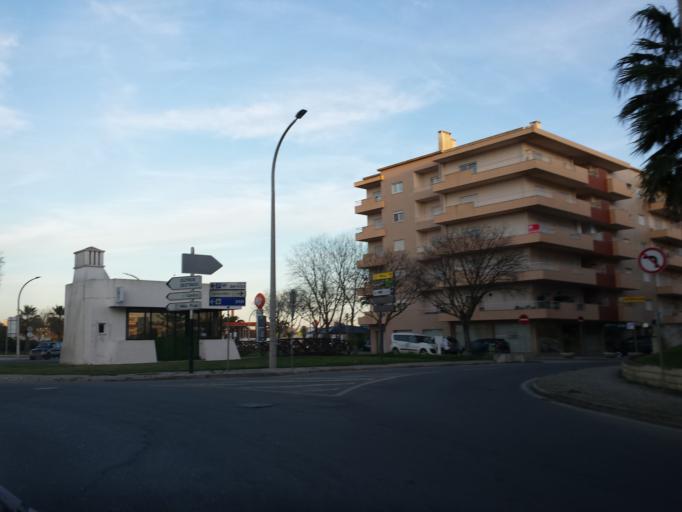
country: PT
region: Faro
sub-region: Lagos
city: Lagos
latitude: 37.1110
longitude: -8.6811
